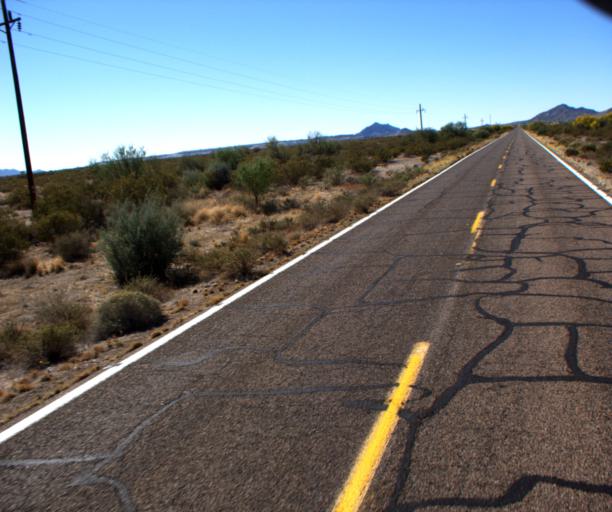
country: US
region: Arizona
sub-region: Pima County
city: Ajo
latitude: 32.4404
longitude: -112.8711
